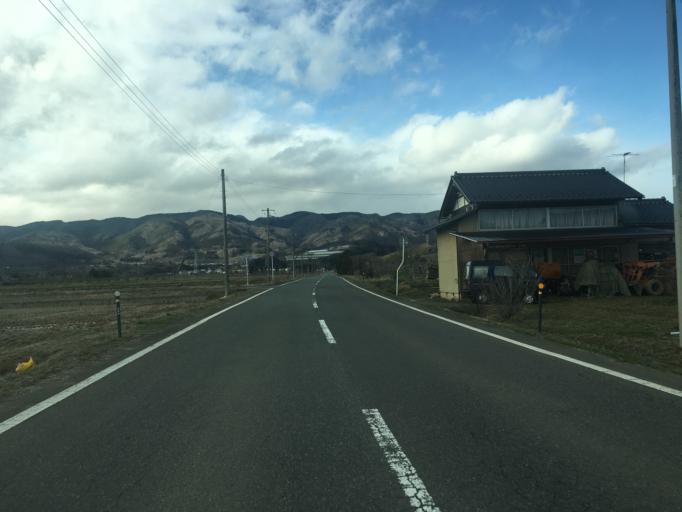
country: JP
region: Fukushima
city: Yanagawamachi-saiwaicho
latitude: 37.8816
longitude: 140.5925
